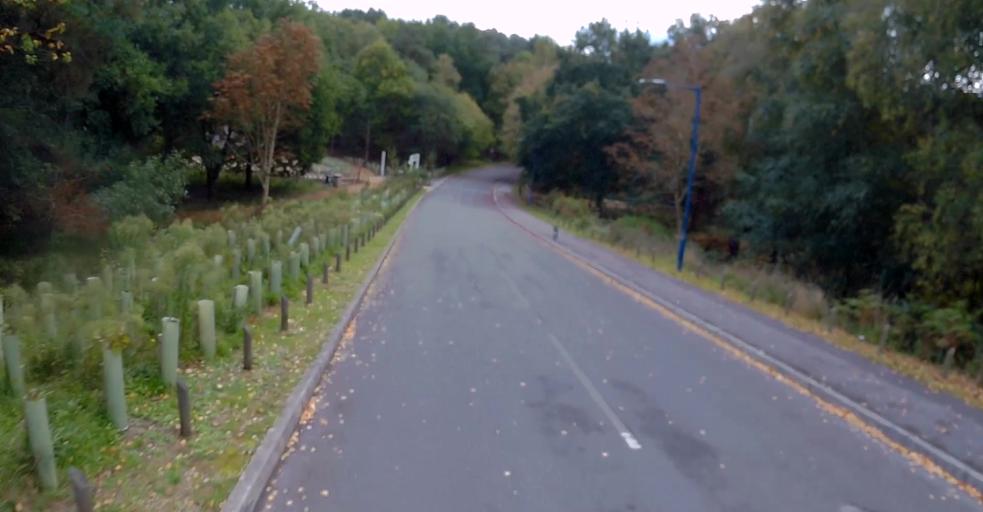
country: GB
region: England
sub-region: Surrey
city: Frimley
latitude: 51.3095
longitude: -0.6994
